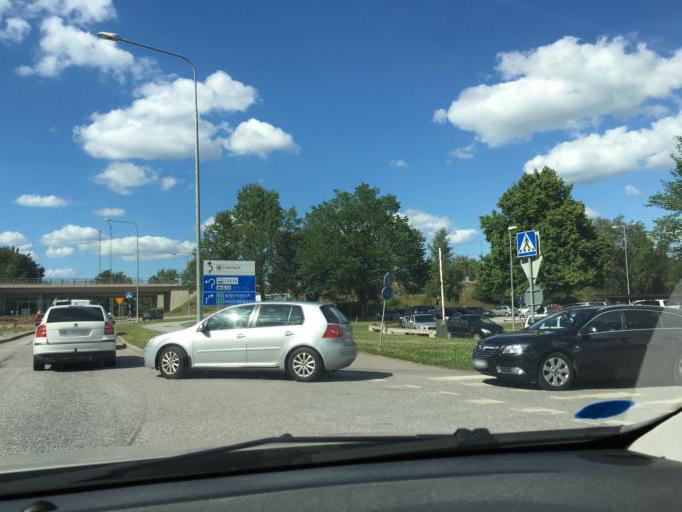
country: SE
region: Stockholm
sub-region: Sodertalje Kommun
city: Soedertaelje
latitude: 59.1752
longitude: 17.6345
